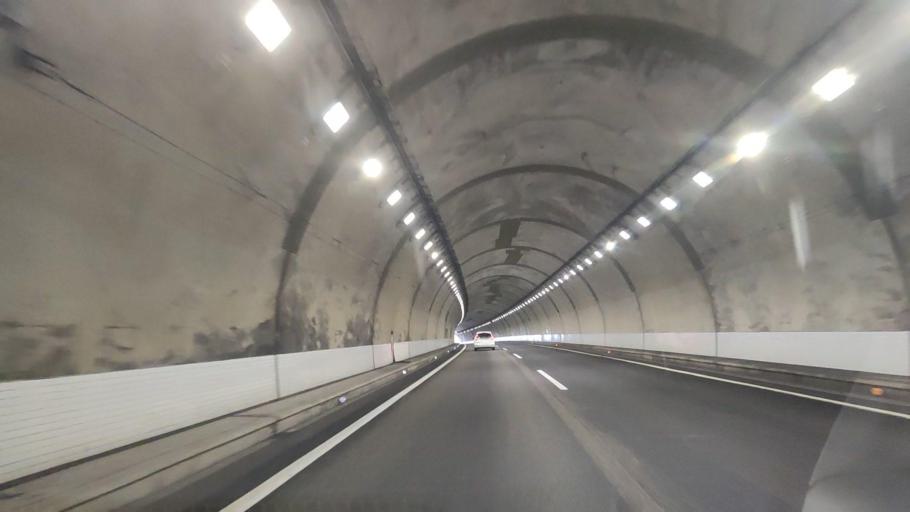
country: JP
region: Niigata
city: Joetsu
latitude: 37.1054
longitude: 138.2201
